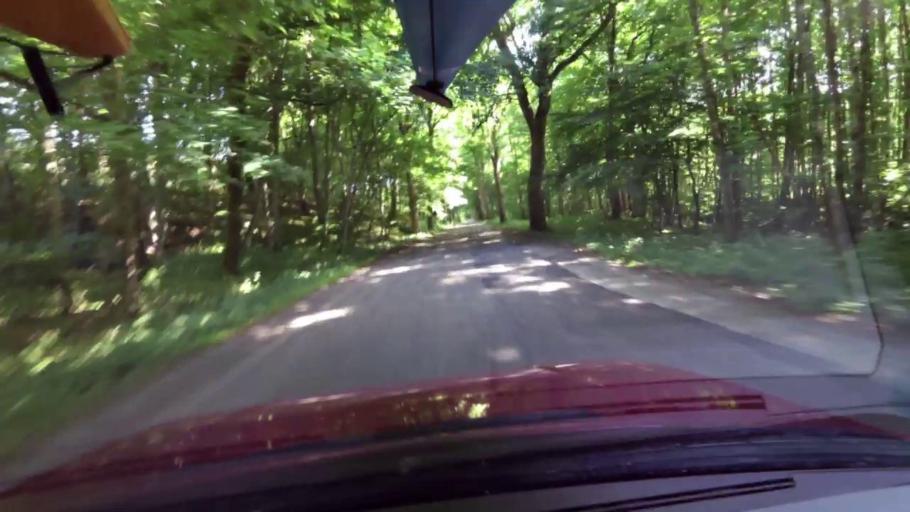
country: PL
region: Pomeranian Voivodeship
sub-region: Powiat slupski
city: Kepice
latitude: 54.1652
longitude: 16.9056
